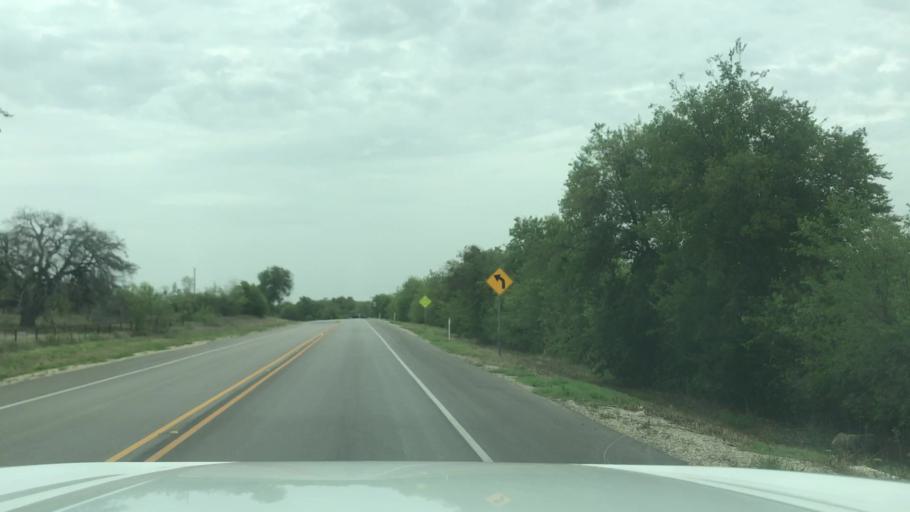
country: US
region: Texas
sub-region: Erath County
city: Dublin
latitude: 32.0618
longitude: -98.2129
